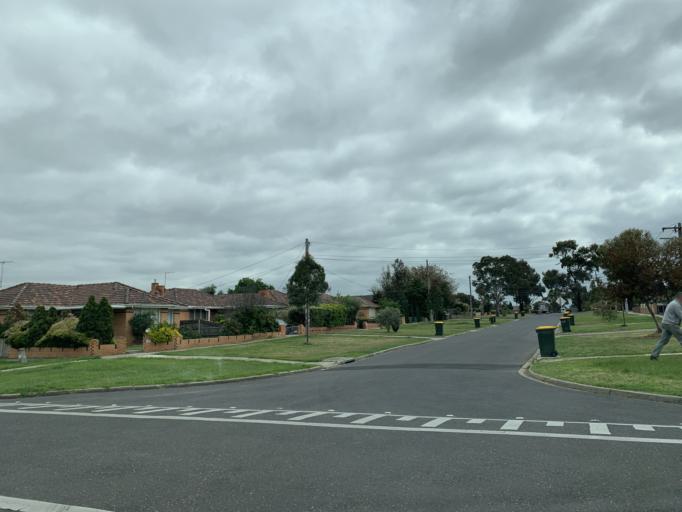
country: AU
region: Victoria
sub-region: Maribyrnong
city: Braybrook
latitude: -37.7695
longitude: 144.8545
